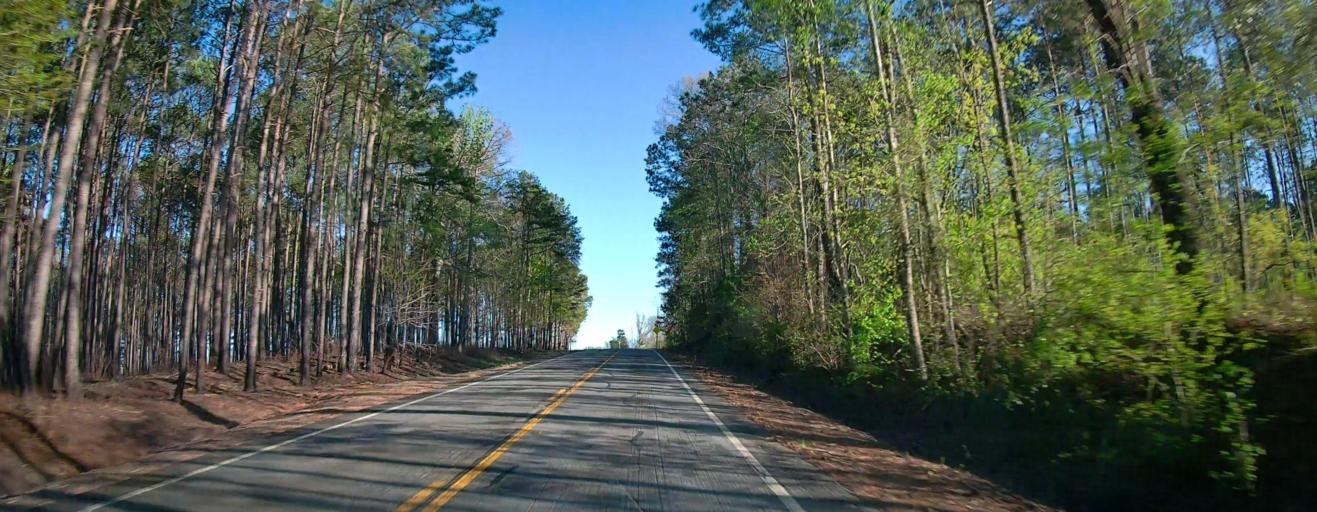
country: US
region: Georgia
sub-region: Wilkinson County
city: Irwinton
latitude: 32.9197
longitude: -83.1299
